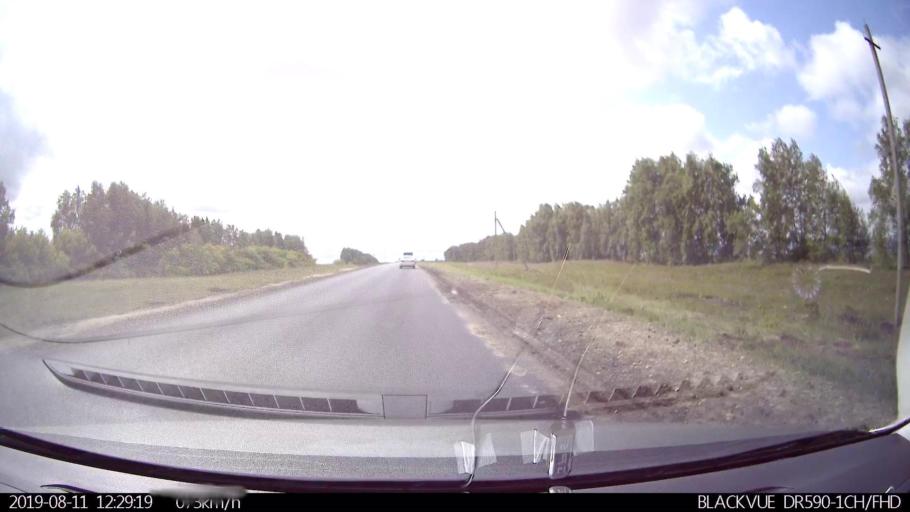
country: RU
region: Ulyanovsk
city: Ignatovka
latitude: 53.8359
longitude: 47.9036
